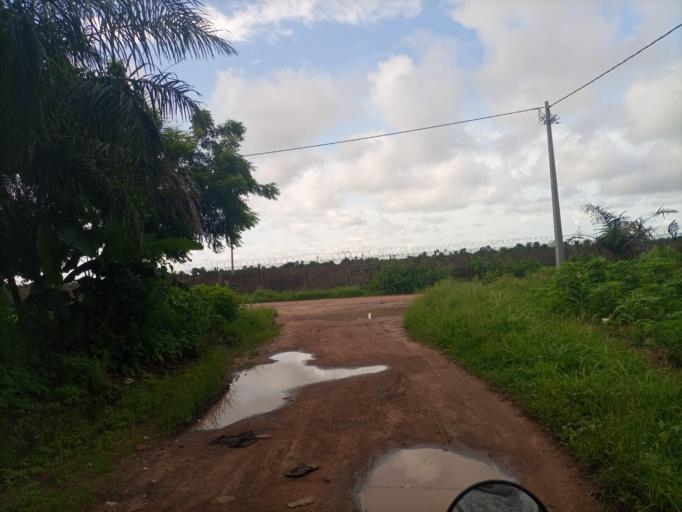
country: SL
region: Northern Province
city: Masoyila
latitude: 8.6102
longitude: -13.1827
